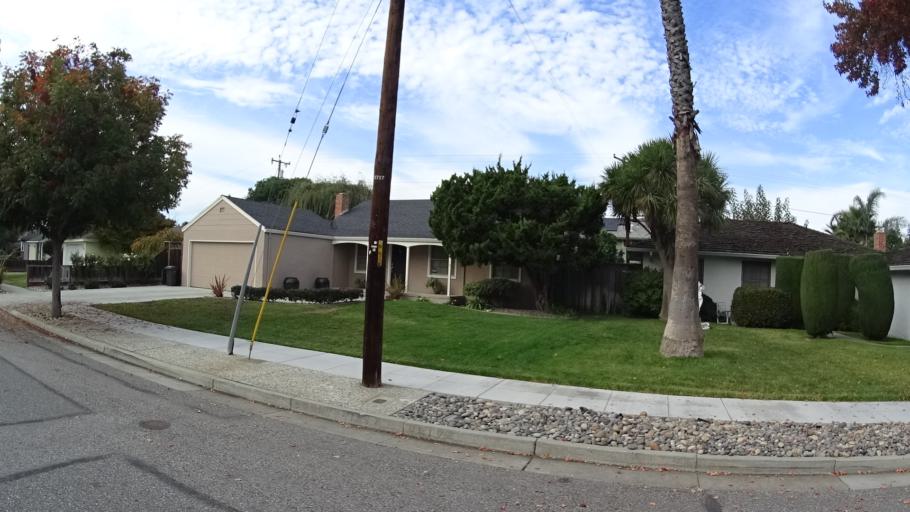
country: US
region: California
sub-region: Santa Clara County
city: Burbank
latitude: 37.3363
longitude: -121.9401
